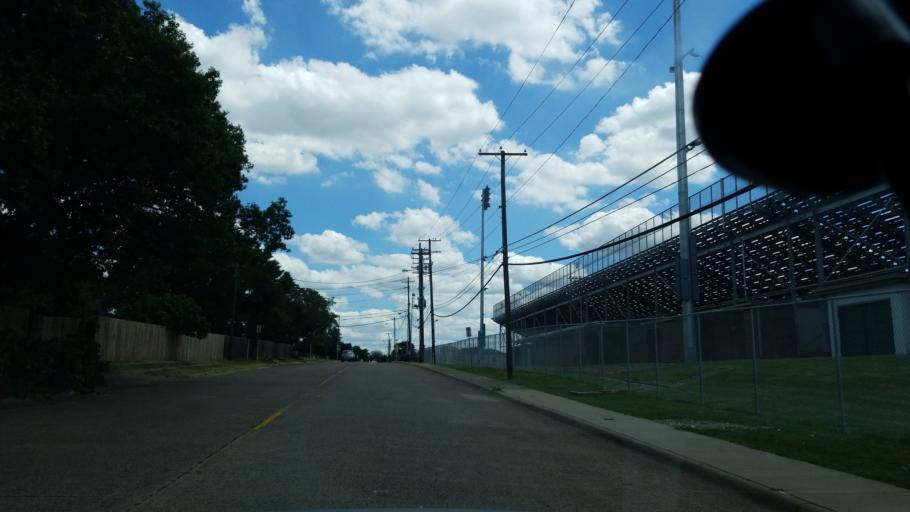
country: US
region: Texas
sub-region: Dallas County
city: Cockrell Hill
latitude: 32.6993
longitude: -96.8743
